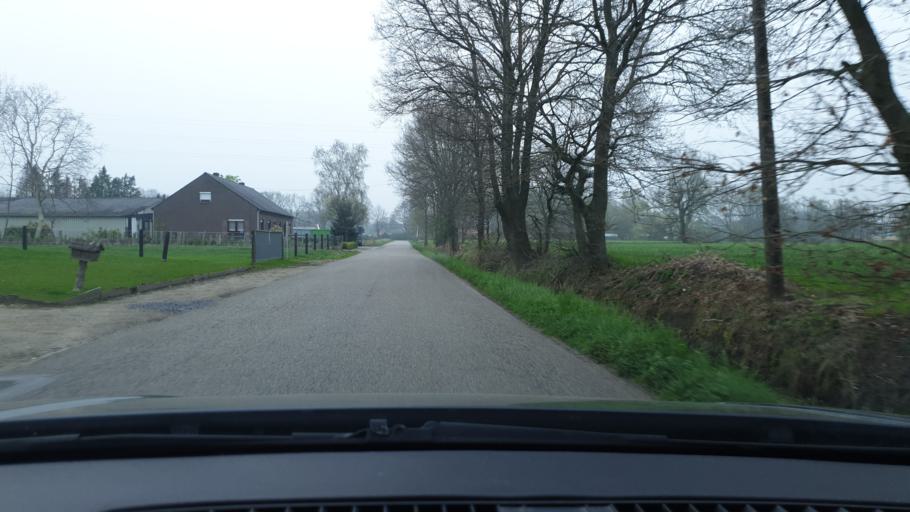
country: BE
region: Flanders
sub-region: Provincie Antwerpen
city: Geel
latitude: 51.1740
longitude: 5.0025
